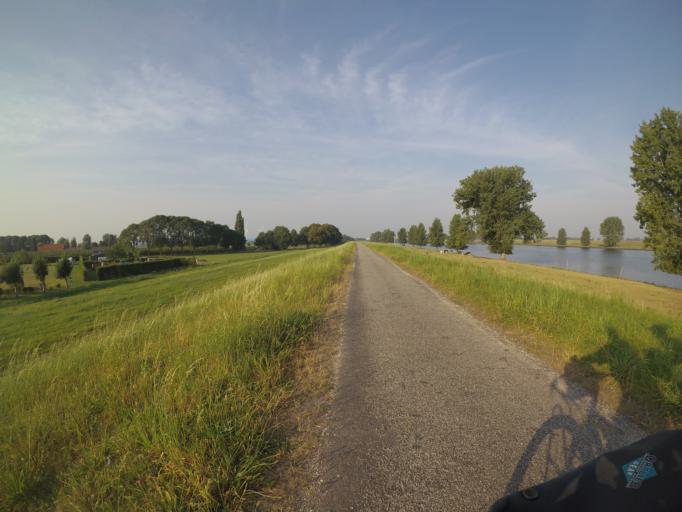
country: NL
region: North Brabant
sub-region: Gemeente Waalwijk
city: Waalwijk
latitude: 51.7240
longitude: 5.0880
